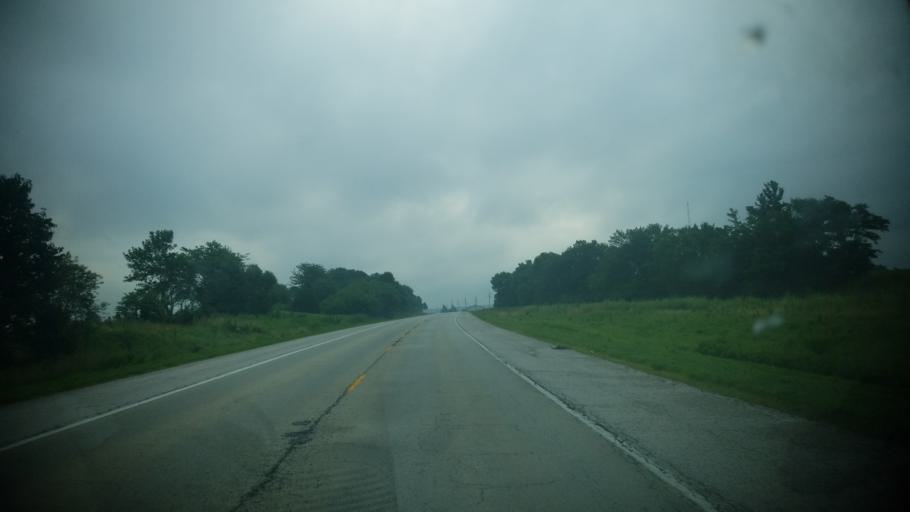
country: US
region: Illinois
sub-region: Clay County
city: Flora
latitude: 38.6775
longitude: -88.3971
